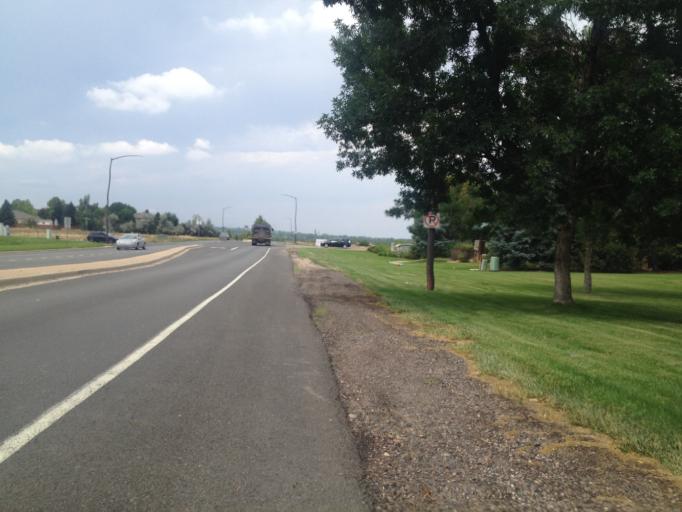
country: US
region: Colorado
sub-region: Boulder County
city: Superior
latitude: 39.9519
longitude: -105.1469
